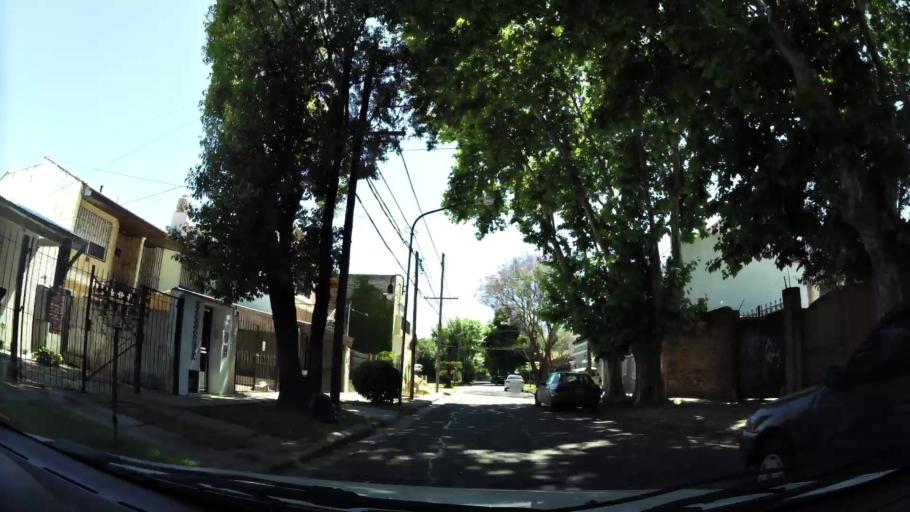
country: AR
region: Buenos Aires
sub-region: Partido de General San Martin
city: General San Martin
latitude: -34.5295
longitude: -58.5410
